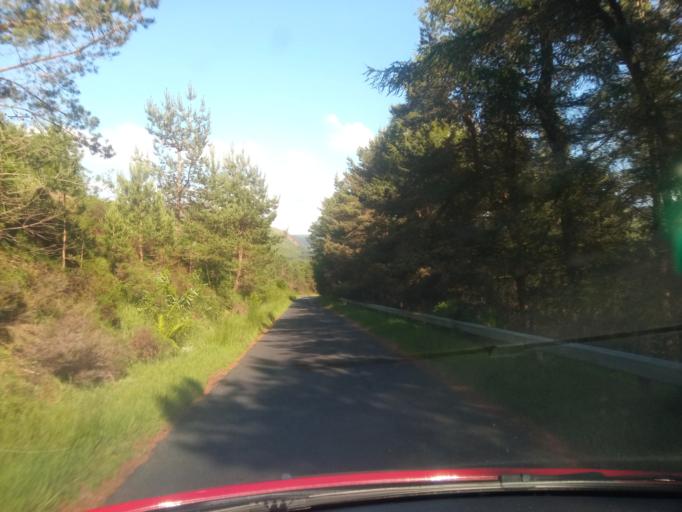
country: GB
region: Scotland
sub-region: The Scottish Borders
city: Peebles
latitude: 55.4964
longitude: -3.2459
